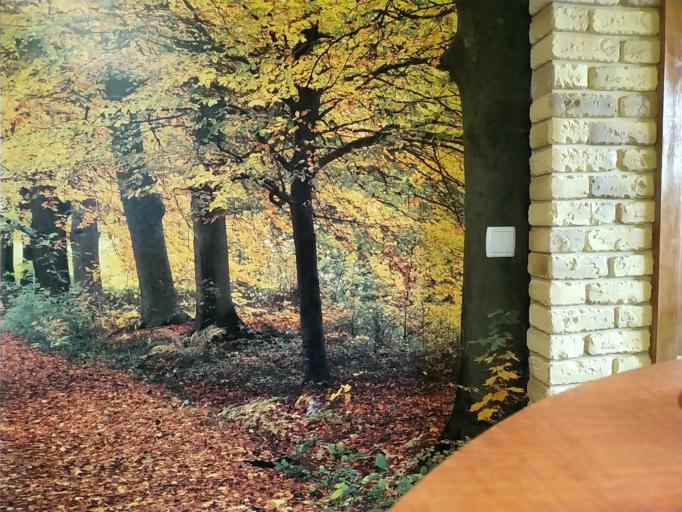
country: RU
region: Novgorod
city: Opechenskiy Posad
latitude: 58.2681
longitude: 34.0213
